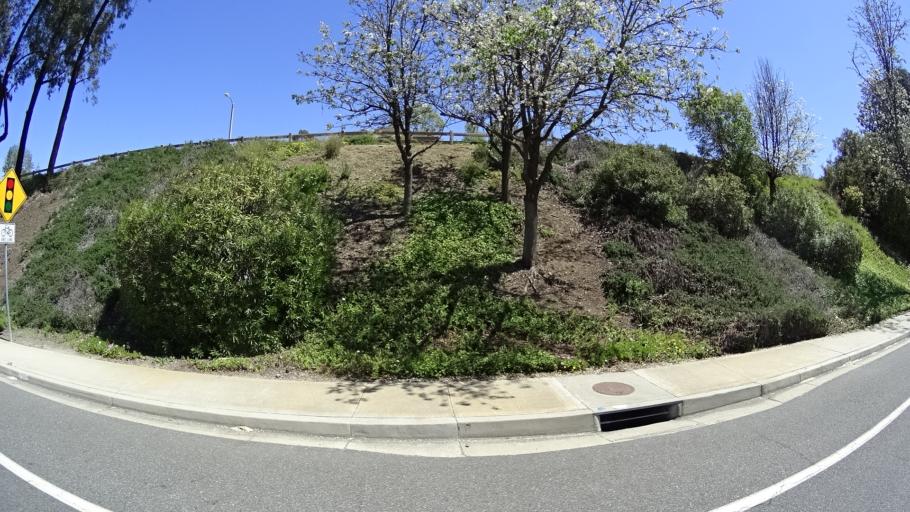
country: US
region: California
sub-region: Ventura County
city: Casa Conejo
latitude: 34.1606
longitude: -118.9466
